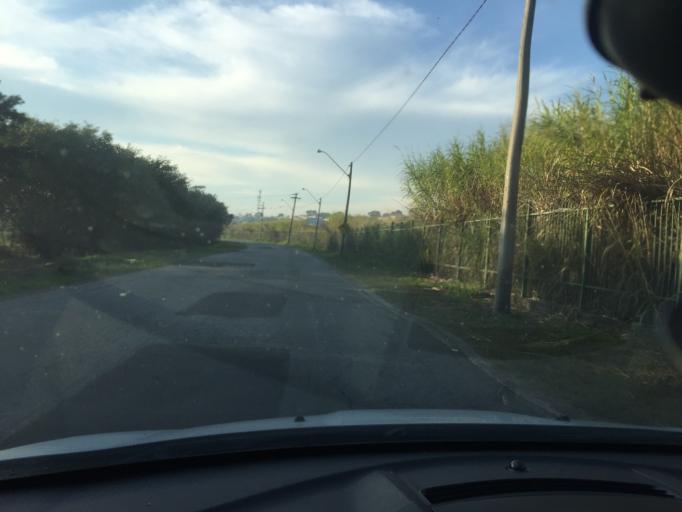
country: BR
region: Sao Paulo
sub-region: Jundiai
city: Jundiai
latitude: -23.2017
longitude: -46.8626
